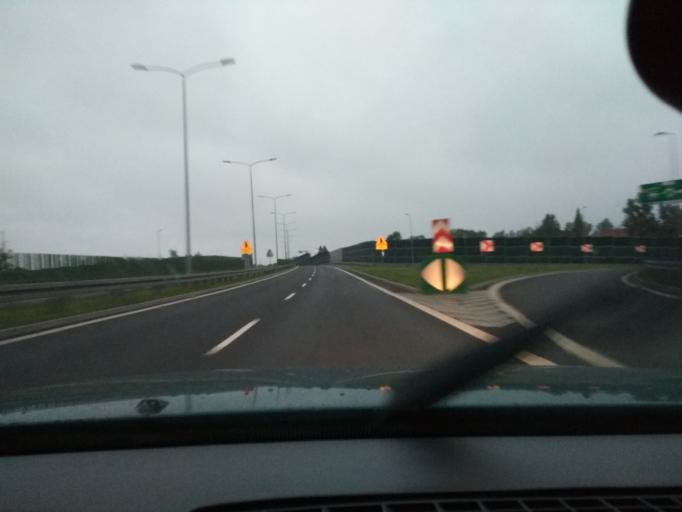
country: PL
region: Silesian Voivodeship
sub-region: Gliwice
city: Gliwice
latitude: 50.2883
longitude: 18.7038
